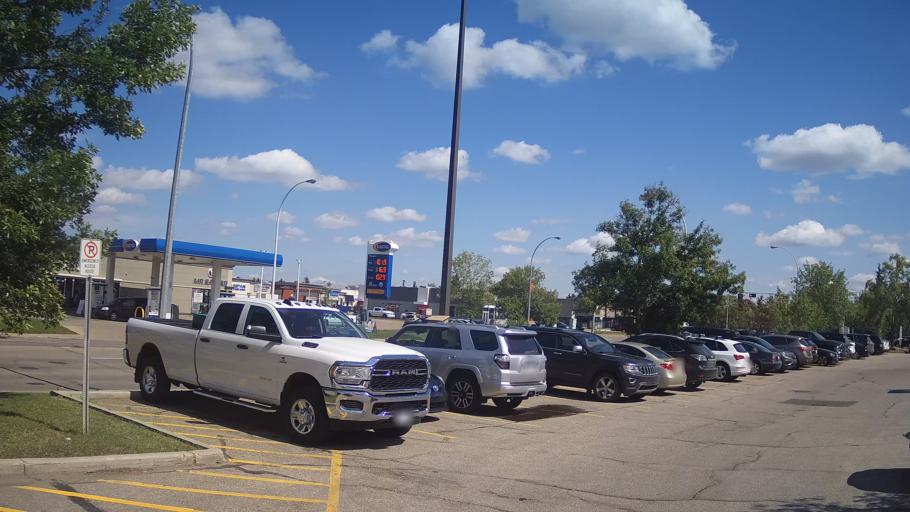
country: CA
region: Alberta
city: St. Albert
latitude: 53.5246
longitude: -113.6192
